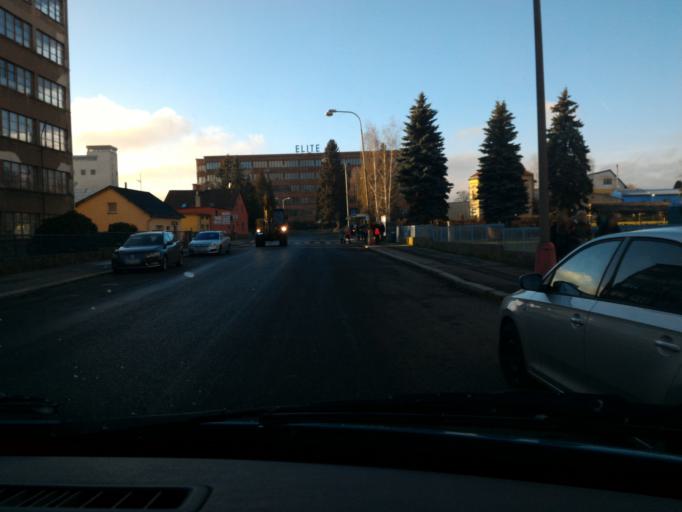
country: CZ
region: Ustecky
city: Varnsdorf
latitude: 50.9105
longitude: 14.6351
